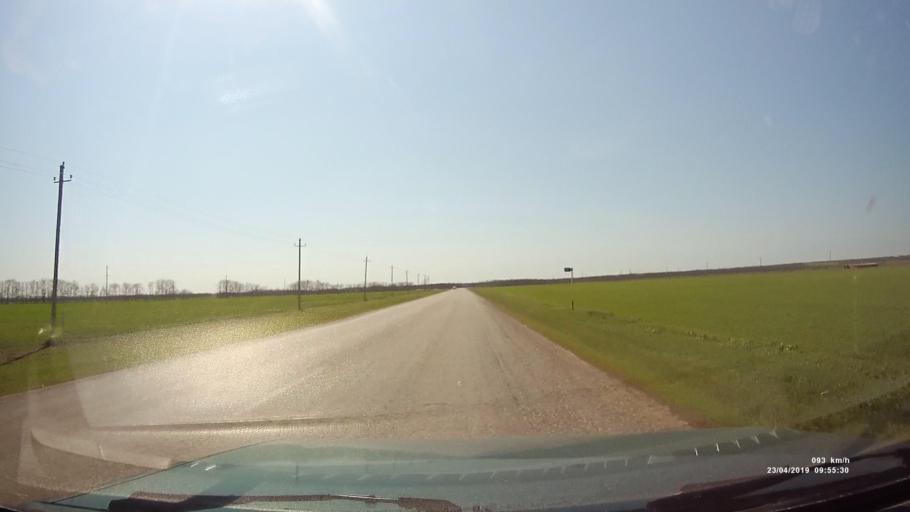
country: RU
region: Rostov
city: Orlovskiy
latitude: 46.8080
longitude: 42.0633
